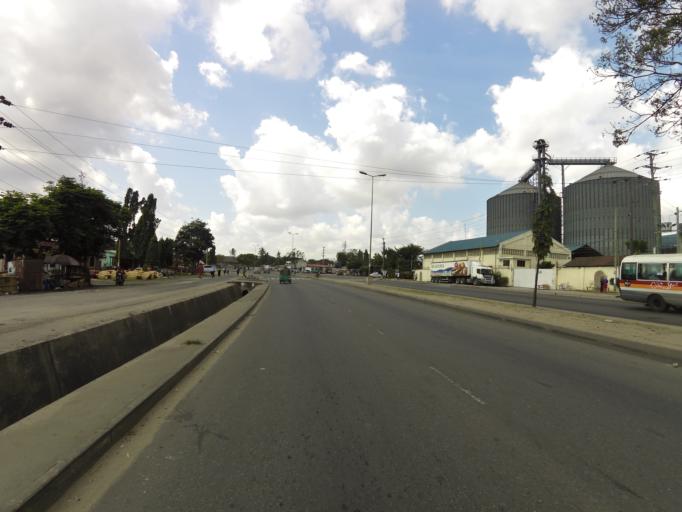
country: TZ
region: Dar es Salaam
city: Magomeni
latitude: -6.8009
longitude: 39.2069
